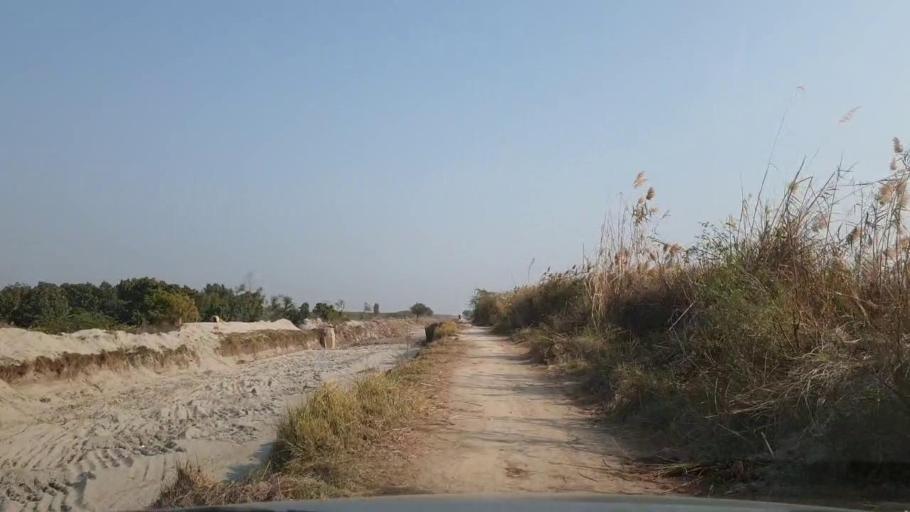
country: PK
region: Sindh
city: Tando Adam
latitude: 25.6482
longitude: 68.5960
